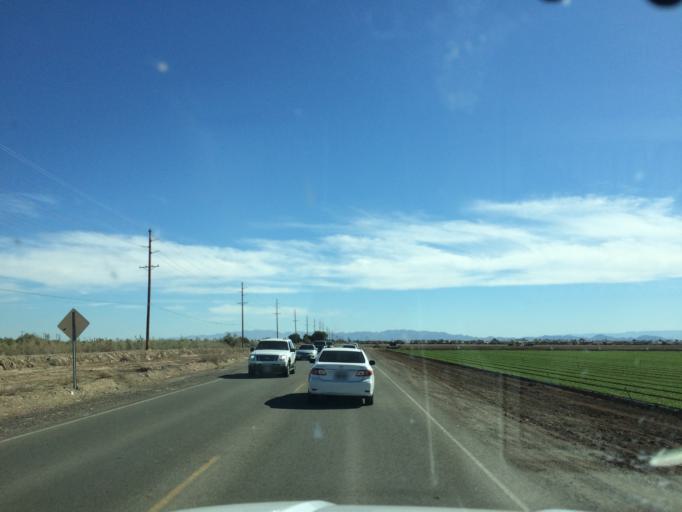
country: US
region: California
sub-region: Imperial County
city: Heber
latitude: 32.7506
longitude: -115.5349
